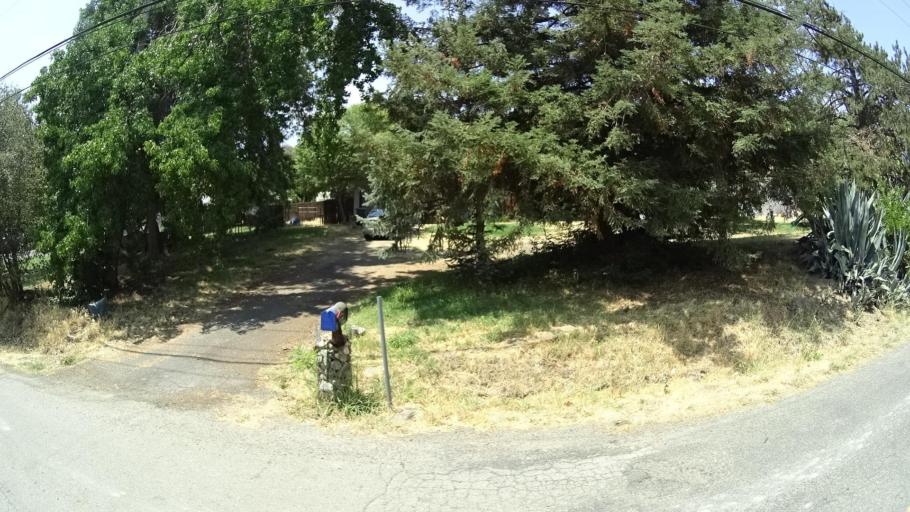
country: US
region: California
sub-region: Placer County
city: Loomis
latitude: 38.8252
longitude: -121.2195
